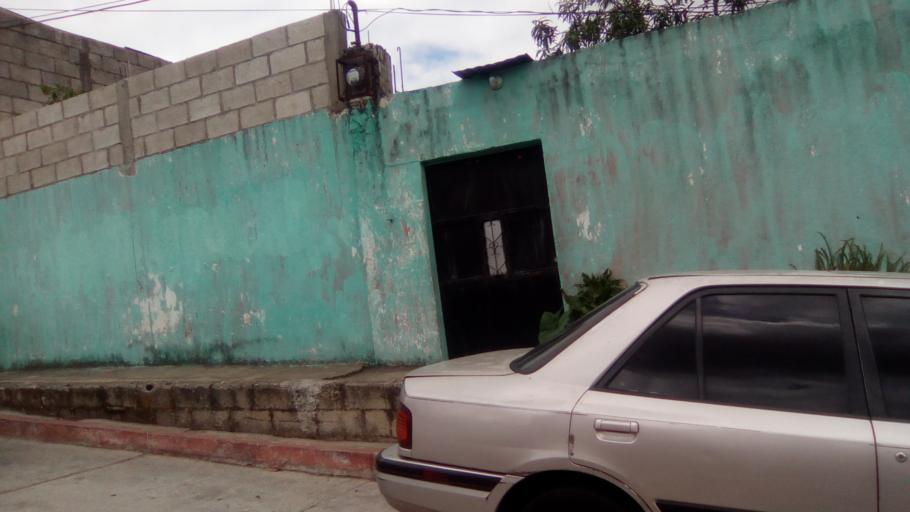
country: GT
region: Guatemala
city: Mixco
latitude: 14.5822
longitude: -90.6043
